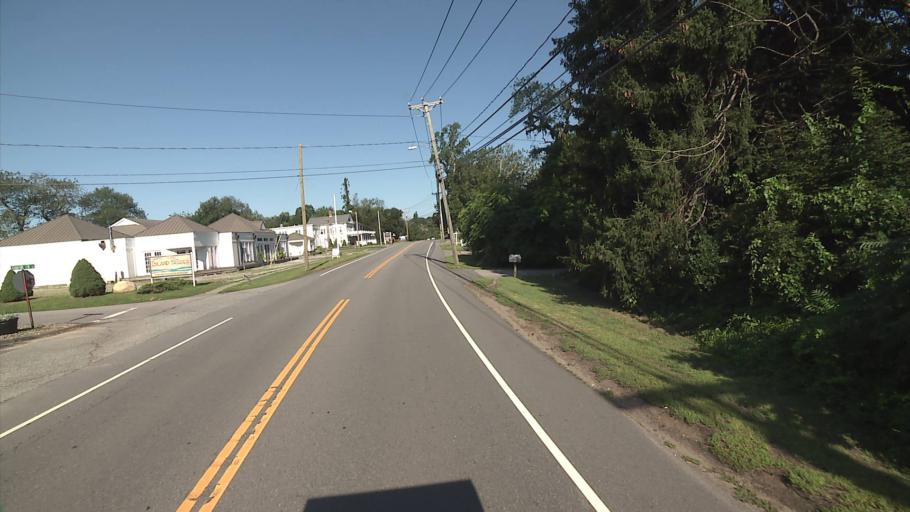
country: US
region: Connecticut
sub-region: Middlesex County
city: Westbrook Center
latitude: 41.2803
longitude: -72.4262
